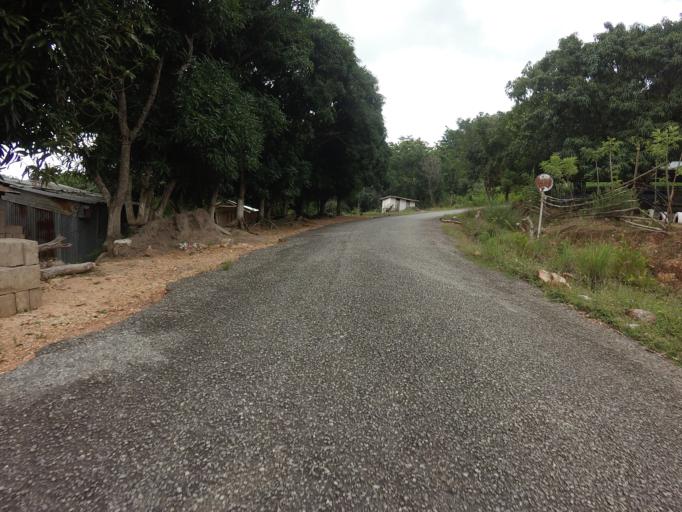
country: GH
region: Volta
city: Kpandu
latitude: 6.8793
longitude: 0.4421
